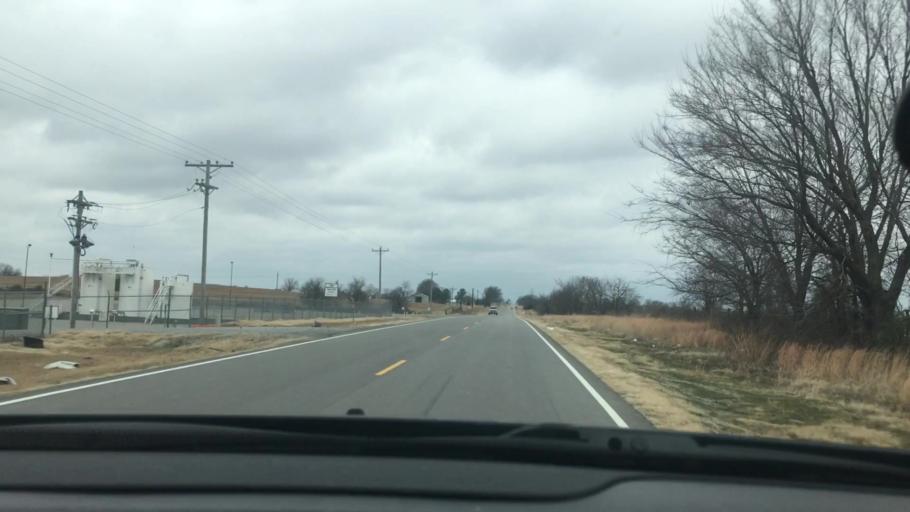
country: US
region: Oklahoma
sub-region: Atoka County
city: Atoka
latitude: 34.3750
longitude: -96.2247
